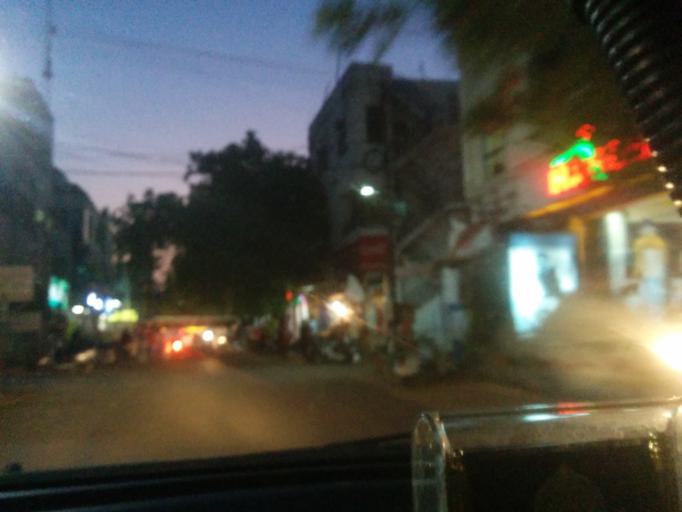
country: IN
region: Andhra Pradesh
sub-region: East Godavari
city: Rajahmundry
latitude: 17.0082
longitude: 81.7810
